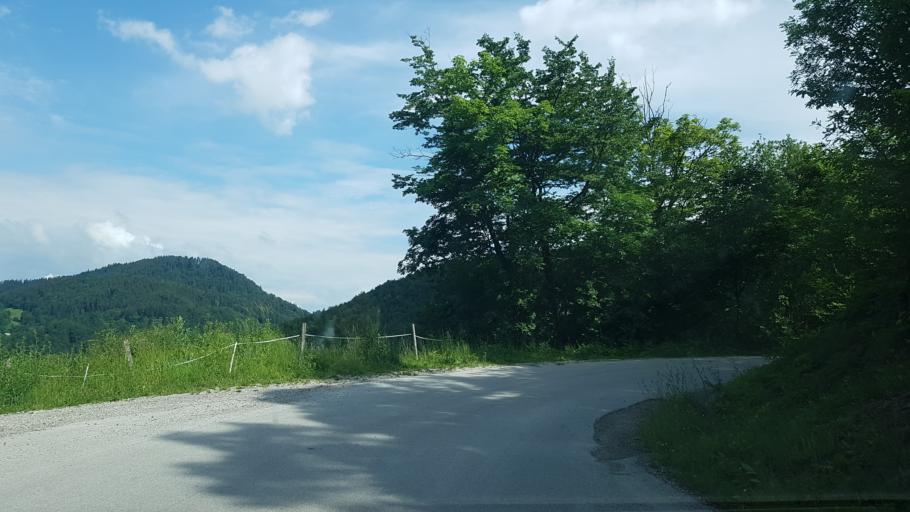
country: SI
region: Velenje
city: Velenje
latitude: 46.3846
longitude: 15.1737
